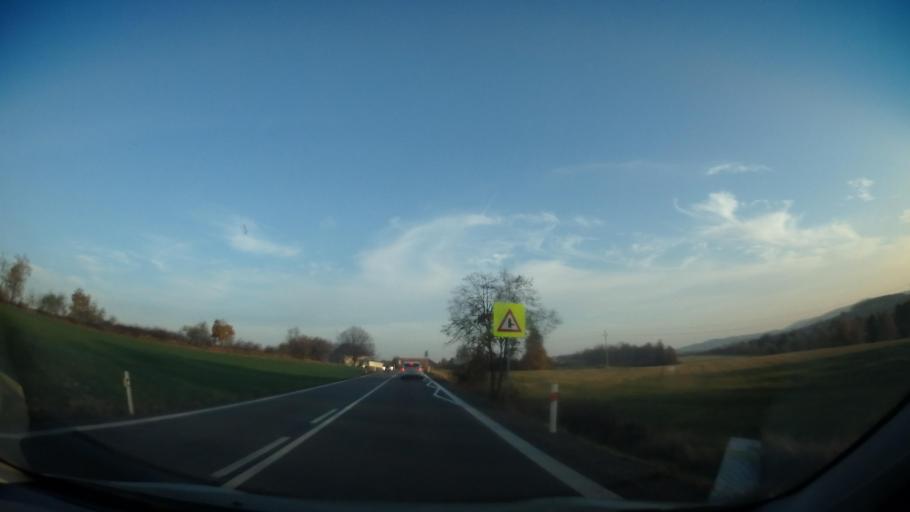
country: CZ
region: Central Bohemia
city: Postupice
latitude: 49.7501
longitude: 14.7759
